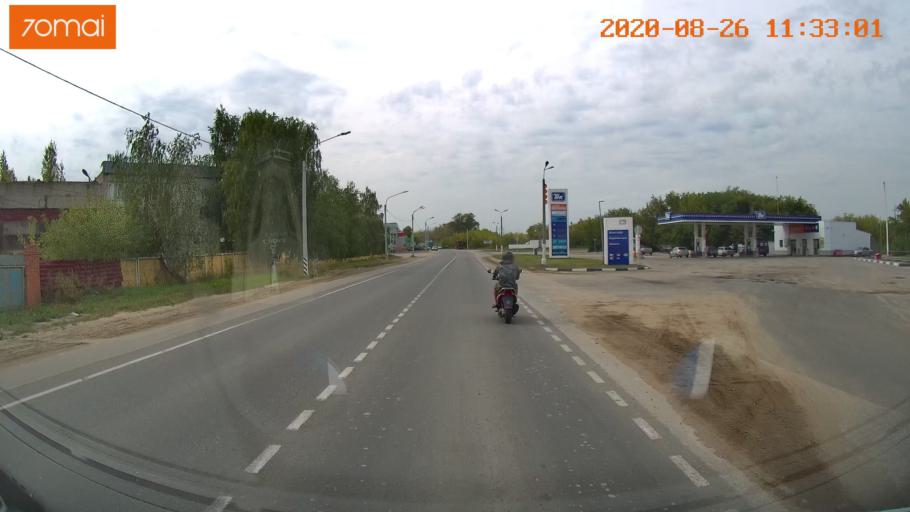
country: RU
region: Rjazan
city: Shilovo
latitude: 54.2988
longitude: 40.8586
